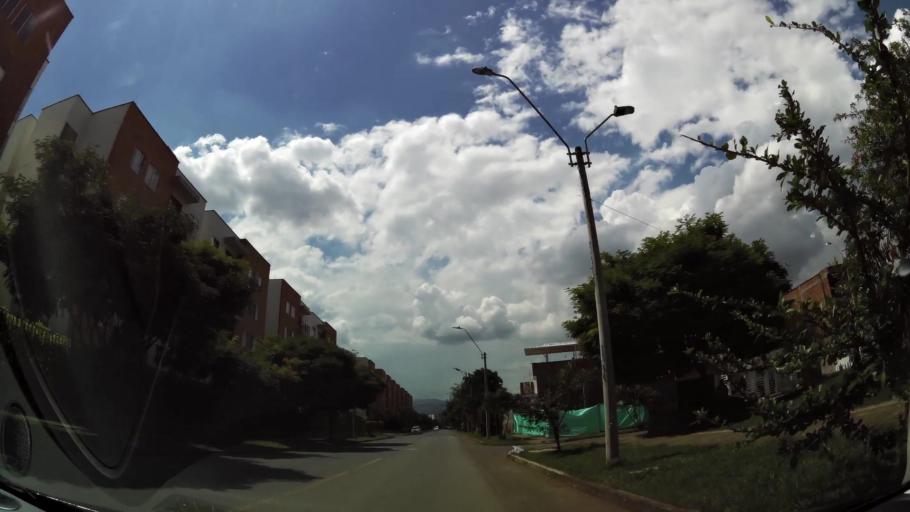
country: CO
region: Valle del Cauca
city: Cali
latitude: 3.3928
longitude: -76.5169
